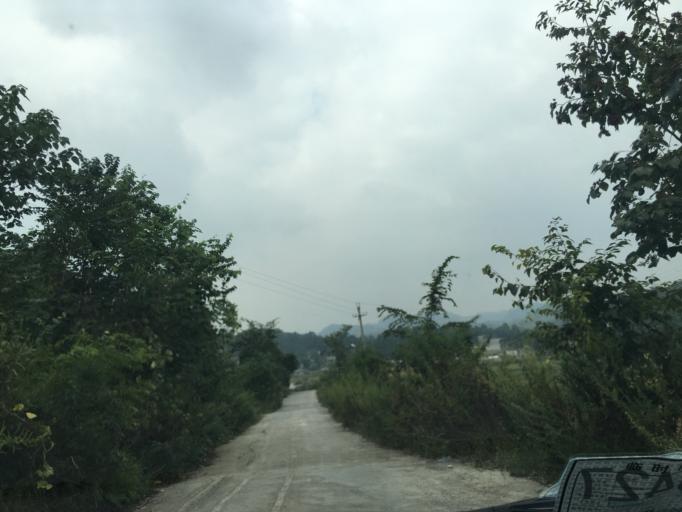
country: CN
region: Guangxi Zhuangzu Zizhiqu
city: Xinzhou
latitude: 25.5670
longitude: 105.6123
